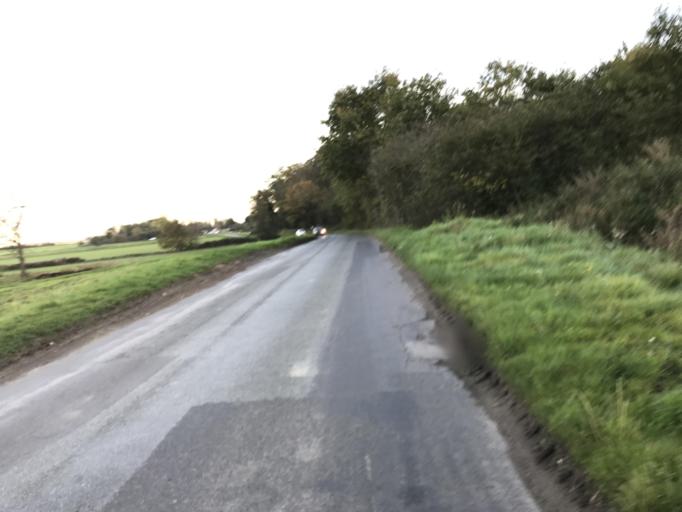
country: FR
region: Ile-de-France
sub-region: Departement de l'Essonne
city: Saulx-les-Chartreux
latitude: 48.6790
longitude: 2.2693
